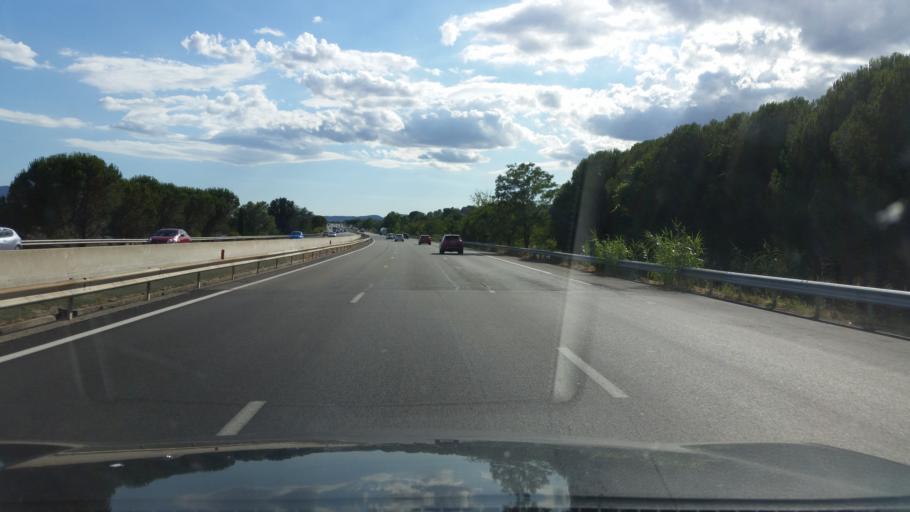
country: FR
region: Provence-Alpes-Cote d'Azur
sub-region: Departement du Var
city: Vidauban
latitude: 43.4124
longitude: 6.4247
